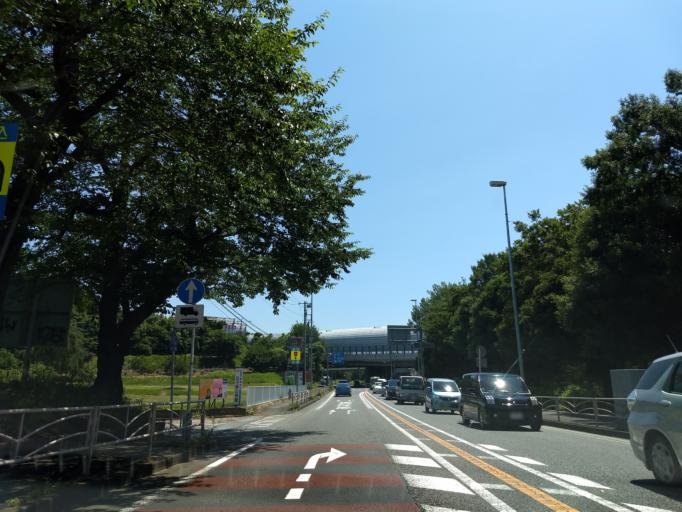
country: JP
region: Kanagawa
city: Isehara
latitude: 35.3905
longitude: 139.2790
